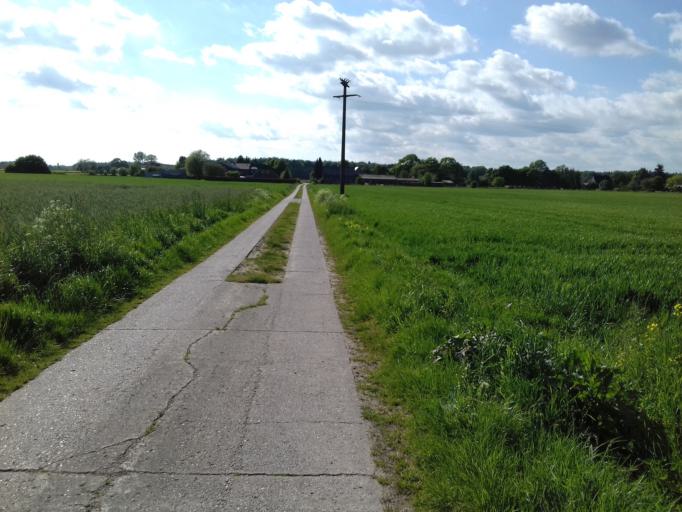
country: DE
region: Schleswig-Holstein
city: Schillsdorf
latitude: 54.0729
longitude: 10.1224
